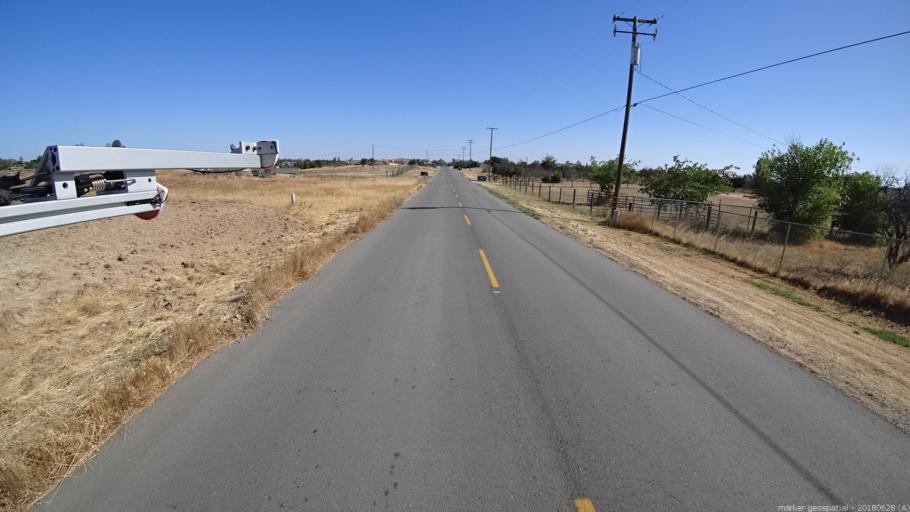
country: US
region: California
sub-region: Madera County
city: Bonadelle Ranchos-Madera Ranchos
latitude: 36.9907
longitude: -119.8794
